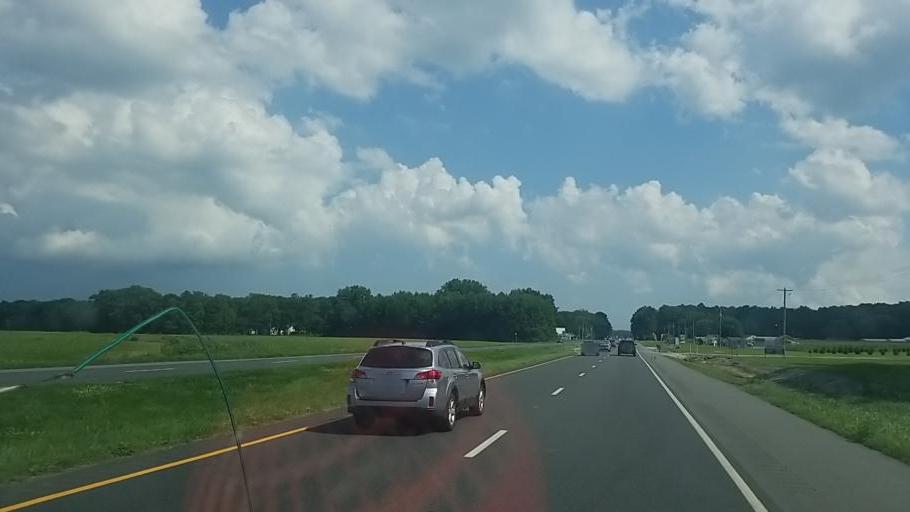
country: US
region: Delaware
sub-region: Sussex County
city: Millsboro
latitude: 38.5344
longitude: -75.2522
